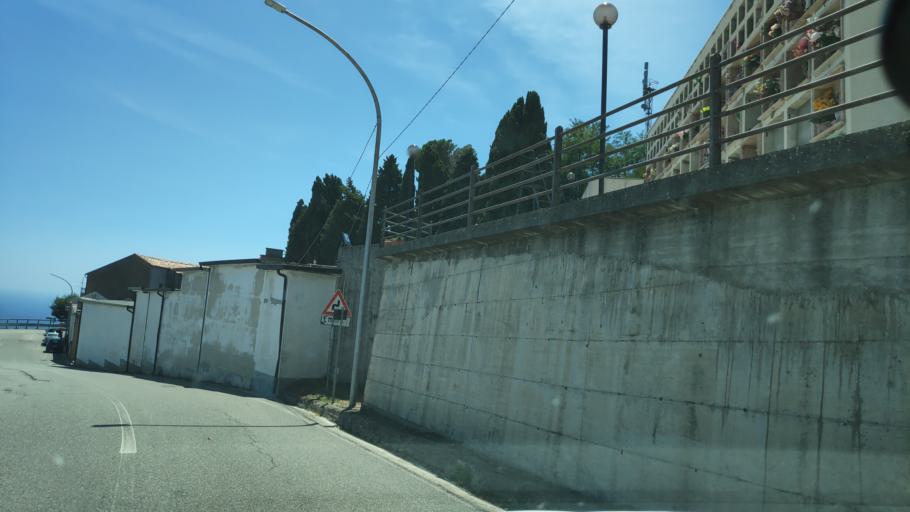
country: IT
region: Calabria
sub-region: Provincia di Catanzaro
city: Gasperina
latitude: 38.7368
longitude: 16.5127
